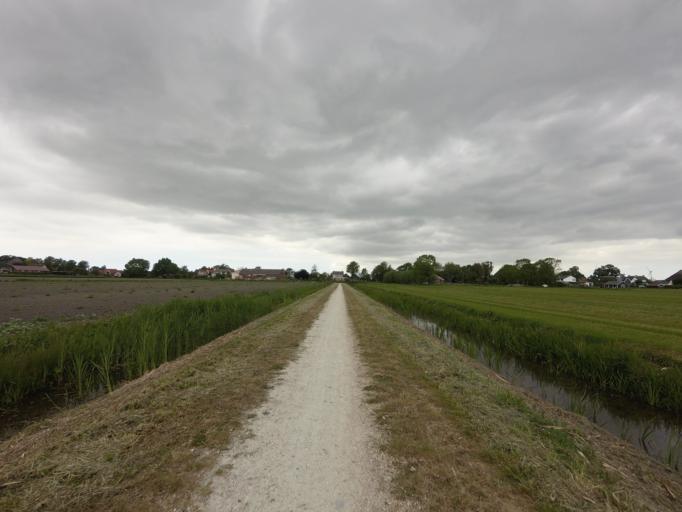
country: NL
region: North Holland
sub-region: Gemeente Hoorn
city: Hoorn
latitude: 52.6155
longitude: 4.9762
